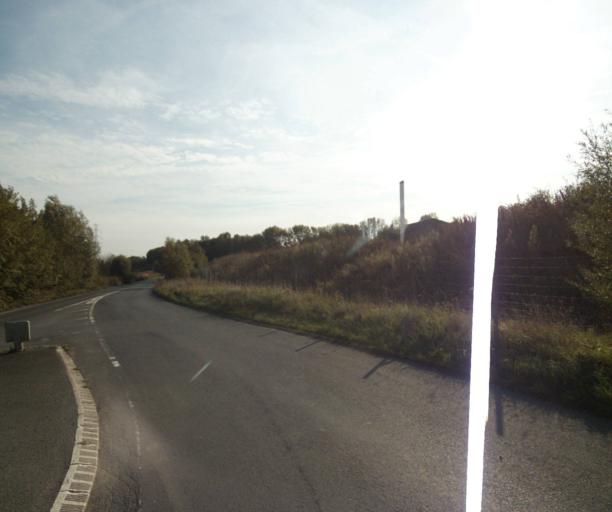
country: FR
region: Nord-Pas-de-Calais
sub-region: Departement du Nord
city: Perenchies
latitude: 50.6565
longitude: 2.9760
